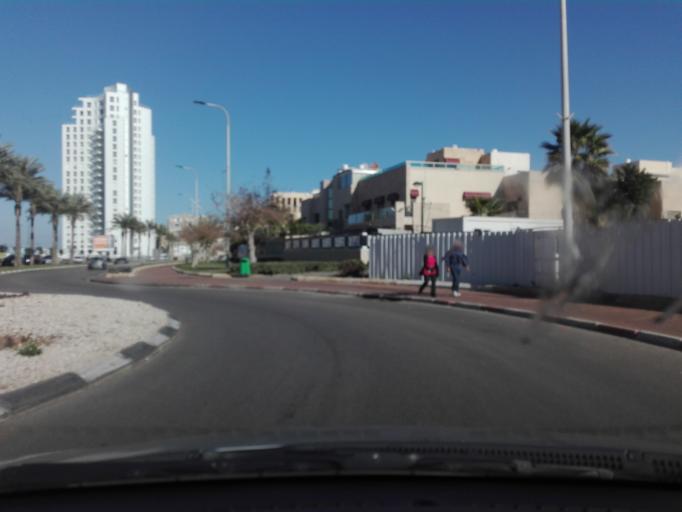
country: IL
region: Central District
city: Netanya
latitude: 32.3167
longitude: 34.8480
